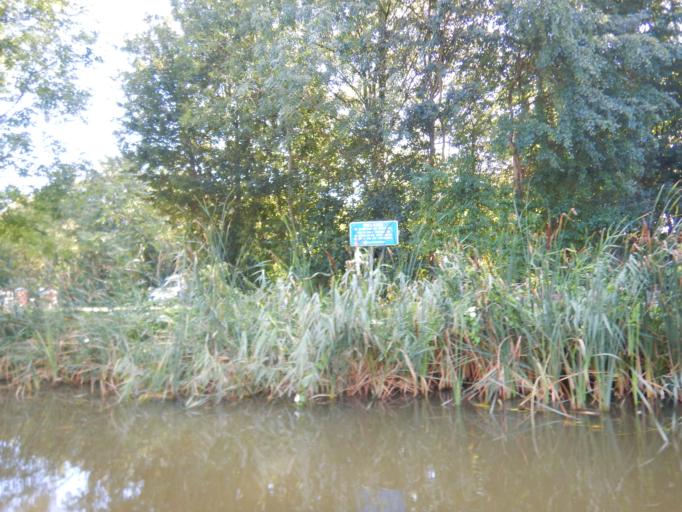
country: NL
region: Groningen
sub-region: Gemeente Winsum
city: Winsum
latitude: 53.3326
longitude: 6.5076
